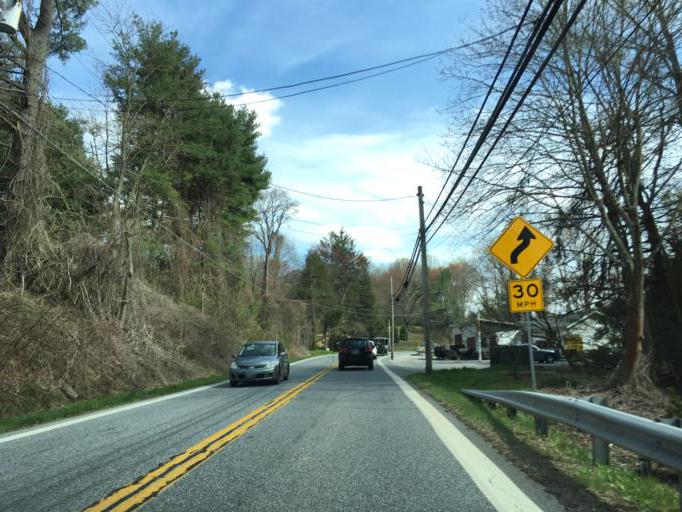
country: US
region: Maryland
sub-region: Baltimore County
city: Mays Chapel
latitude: 39.4542
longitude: -76.6899
